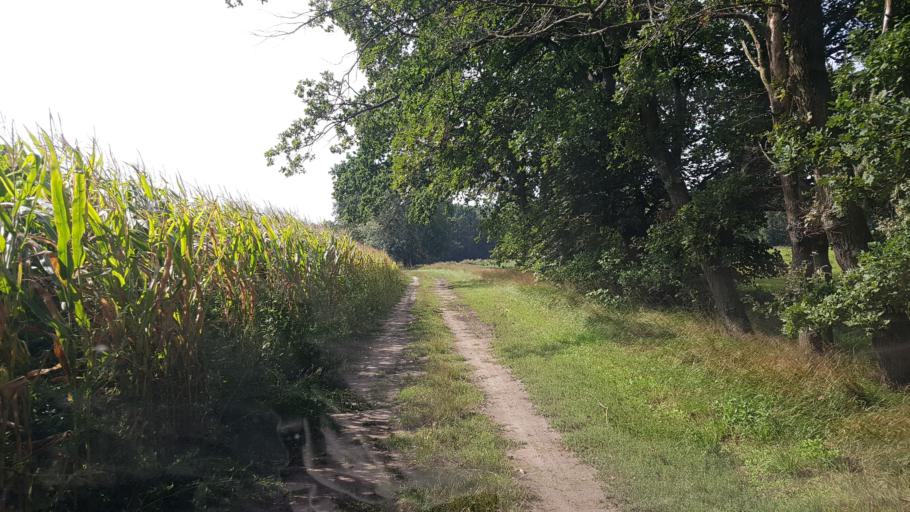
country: DE
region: Brandenburg
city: Hohenbucko
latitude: 51.7207
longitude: 13.4832
